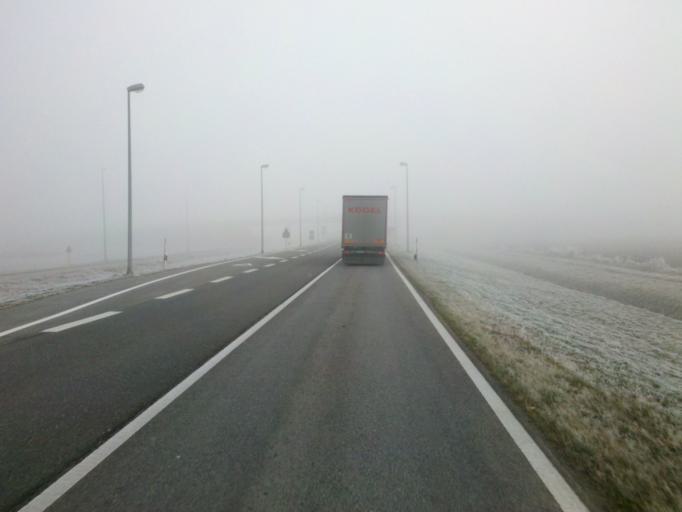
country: HR
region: Varazdinska
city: Varazdin
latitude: 46.2649
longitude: 16.3780
